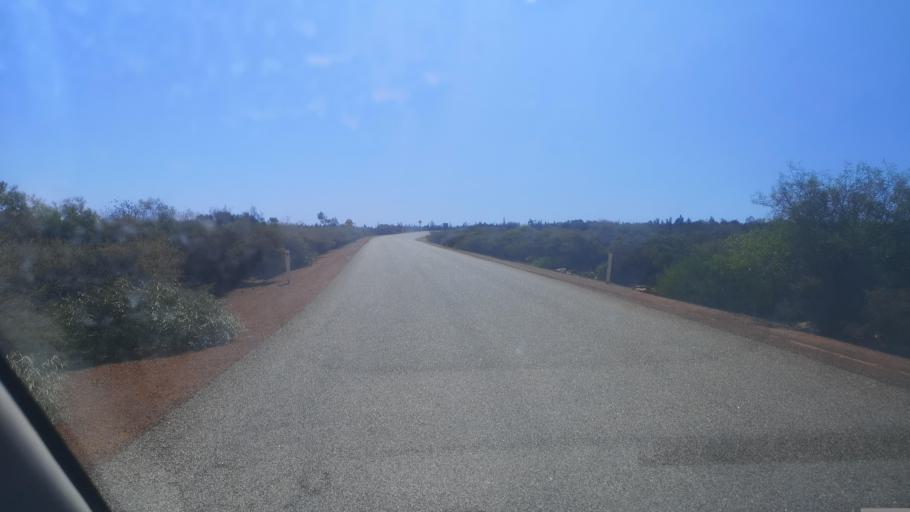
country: AU
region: Western Australia
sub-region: Northampton Shire
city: Kalbarri
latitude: -27.8168
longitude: 114.4677
